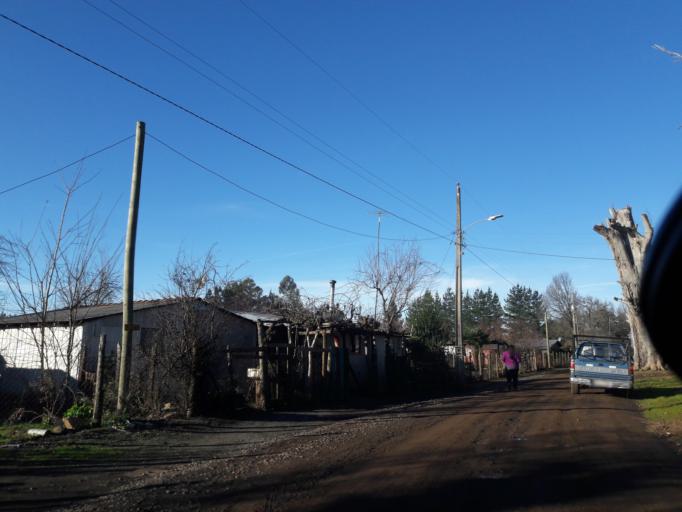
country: CL
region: Biobio
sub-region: Provincia de Biobio
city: Cabrero
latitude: -37.0098
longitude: -72.1833
